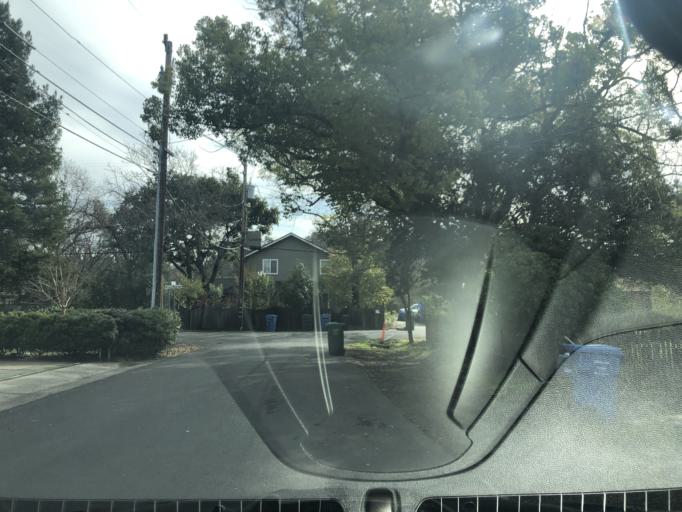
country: US
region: California
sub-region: Contra Costa County
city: Saranap
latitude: 37.8883
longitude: -122.0750
